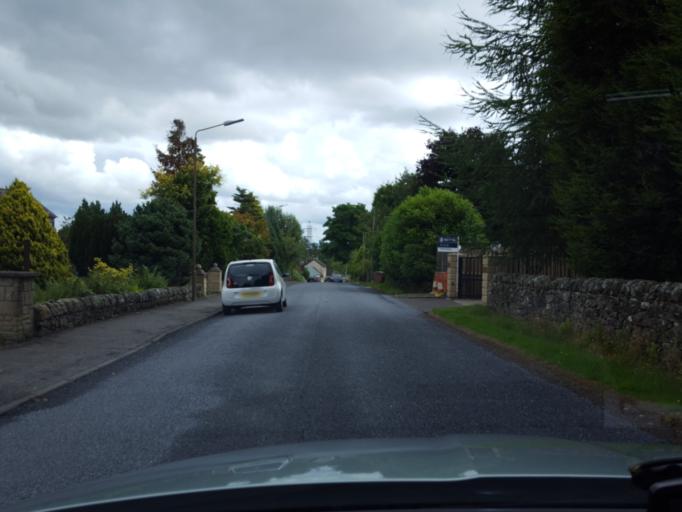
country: GB
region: Scotland
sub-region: Stirling
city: Cowie
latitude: 56.0433
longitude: -3.8644
